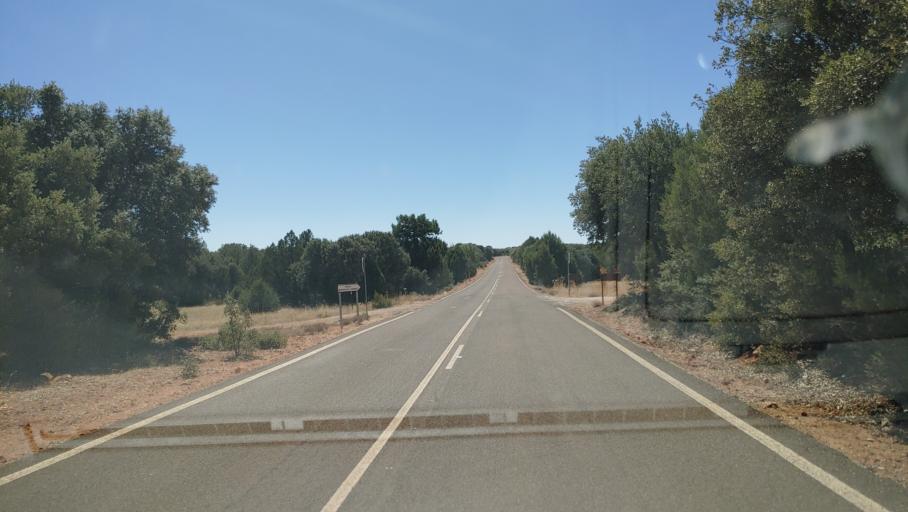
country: ES
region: Castille-La Mancha
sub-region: Provincia de Ciudad Real
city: Villahermosa
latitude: 38.8381
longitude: -2.8169
